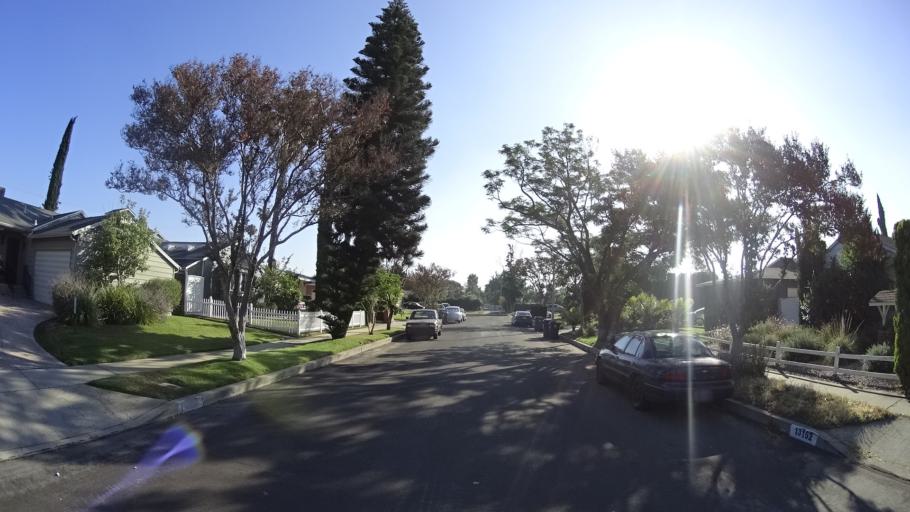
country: US
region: California
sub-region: Los Angeles County
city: San Fernando
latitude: 34.2341
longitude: -118.4192
